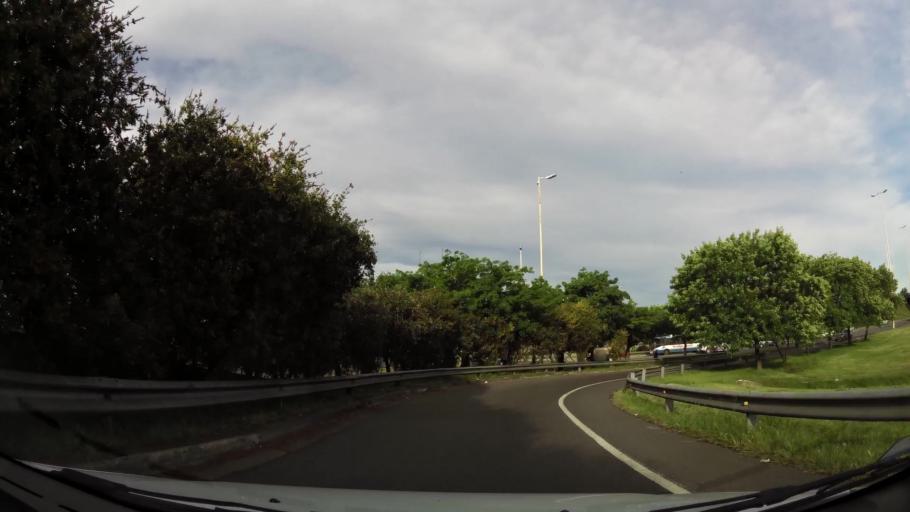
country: AR
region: Buenos Aires
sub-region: Partido de Moron
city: Moron
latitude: -34.6316
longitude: -58.6308
